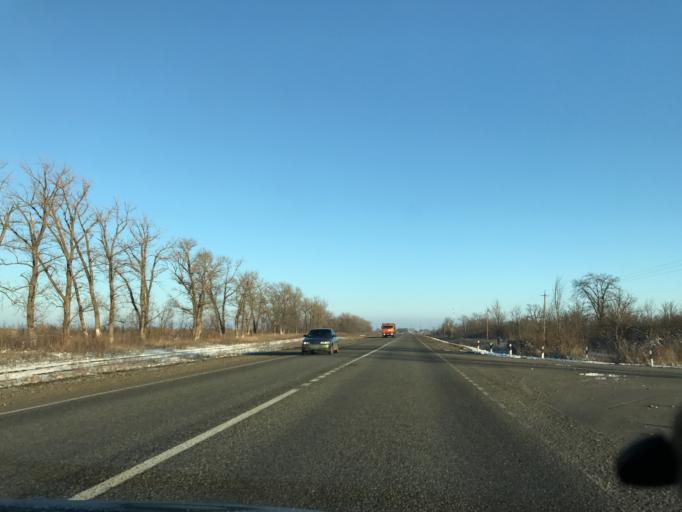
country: RU
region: Stavropol'skiy
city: Bezopasnoye
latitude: 45.6034
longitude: 41.9416
